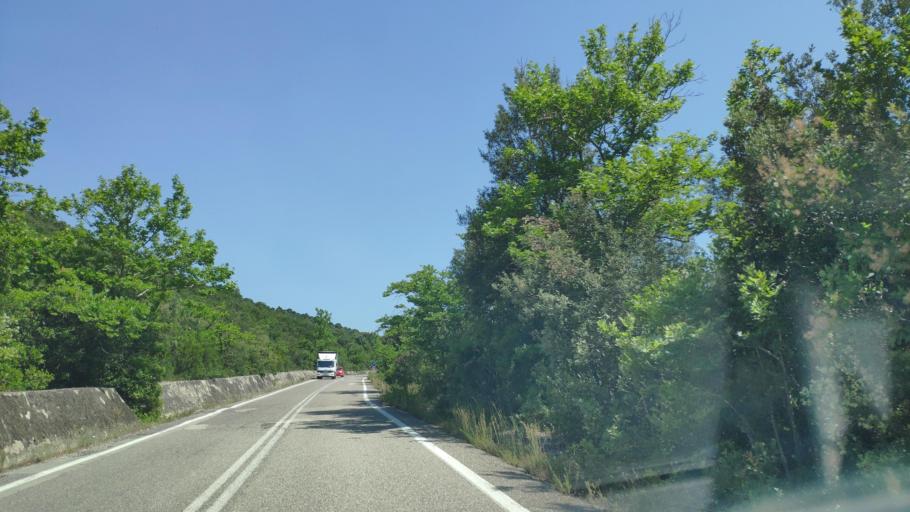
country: GR
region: West Greece
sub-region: Nomos Aitolias kai Akarnanias
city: Lepenou
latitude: 38.7801
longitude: 21.3351
